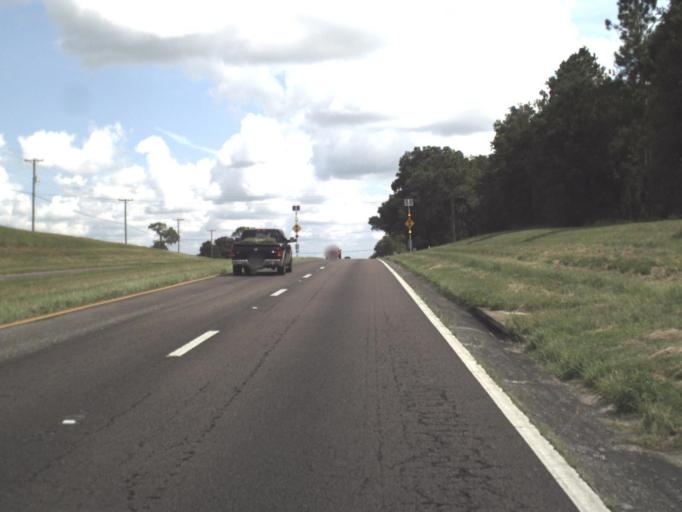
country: US
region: Florida
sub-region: Pasco County
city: Zephyrhills North
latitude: 28.2963
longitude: -82.1877
